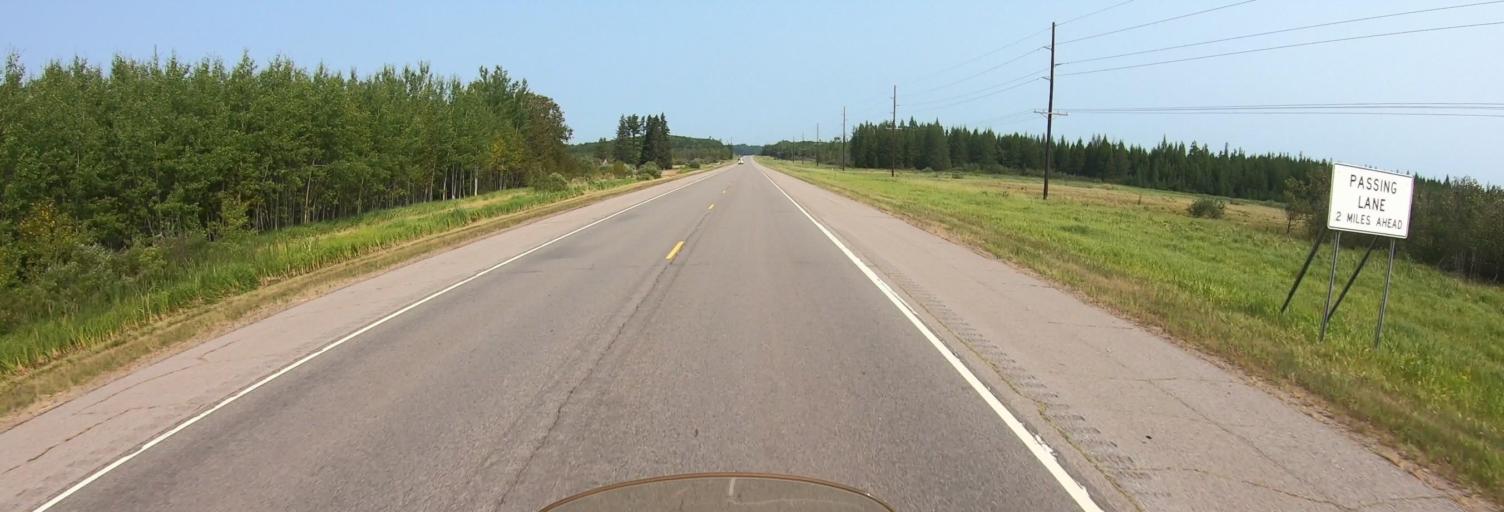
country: US
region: Minnesota
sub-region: Saint Louis County
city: Chisholm
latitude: 47.9431
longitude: -92.8289
